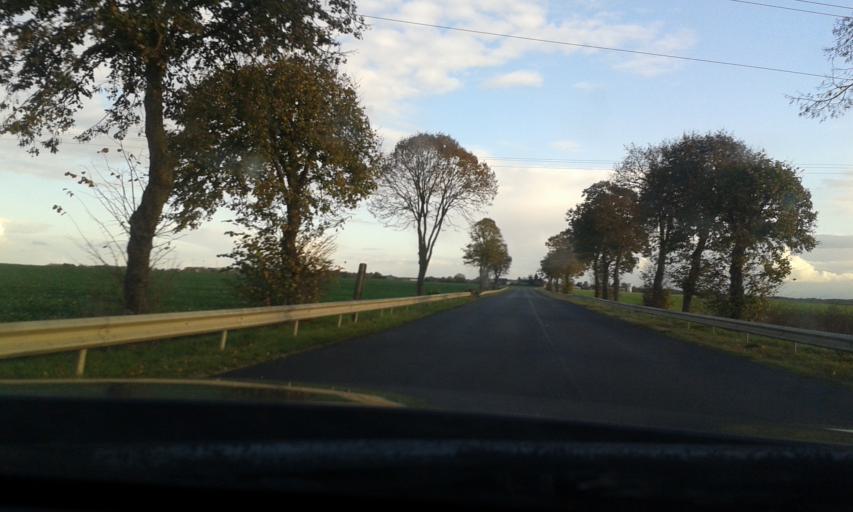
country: FR
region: Centre
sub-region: Departement d'Eure-et-Loir
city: Le Coudray
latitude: 48.4237
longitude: 1.5216
